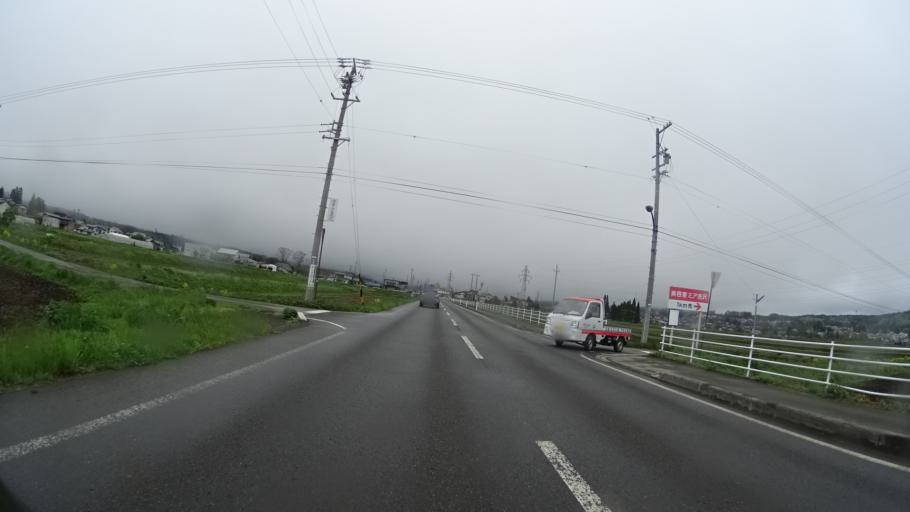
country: JP
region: Nagano
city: Nagano-shi
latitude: 36.7990
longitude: 138.1951
